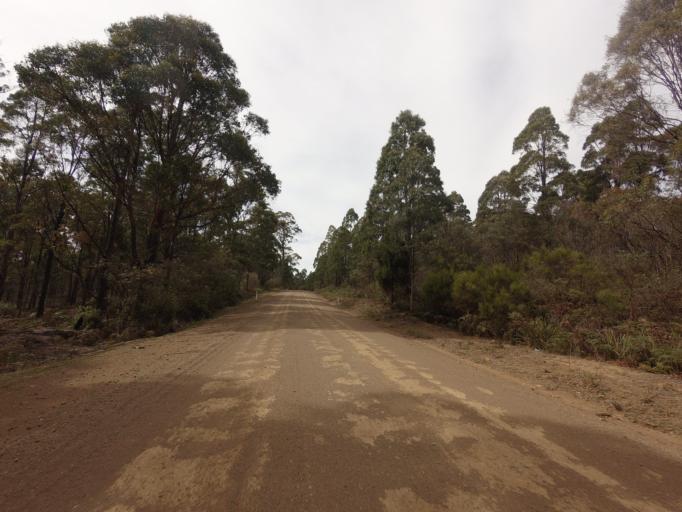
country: AU
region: Tasmania
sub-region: Sorell
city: Sorell
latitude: -42.4919
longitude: 147.6234
